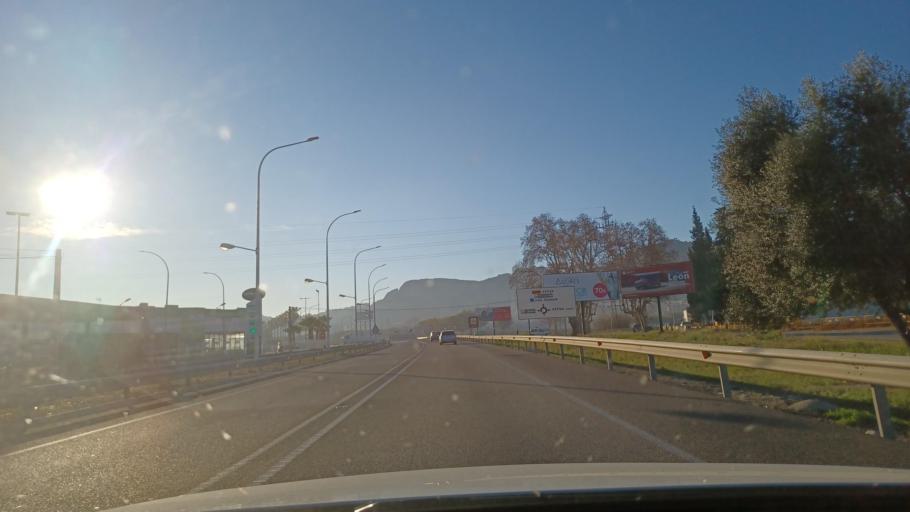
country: ES
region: Valencia
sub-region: Provincia de Valencia
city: Xativa
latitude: 39.0004
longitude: -0.5276
